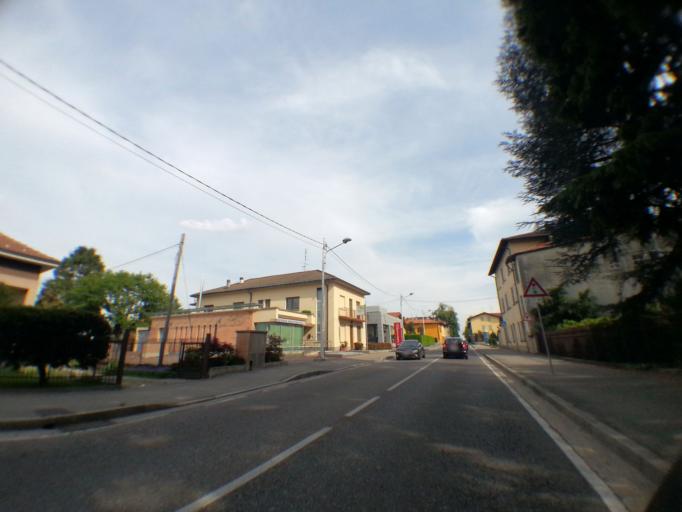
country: IT
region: Lombardy
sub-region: Provincia di Como
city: Cermenate
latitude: 45.7128
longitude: 9.0812
